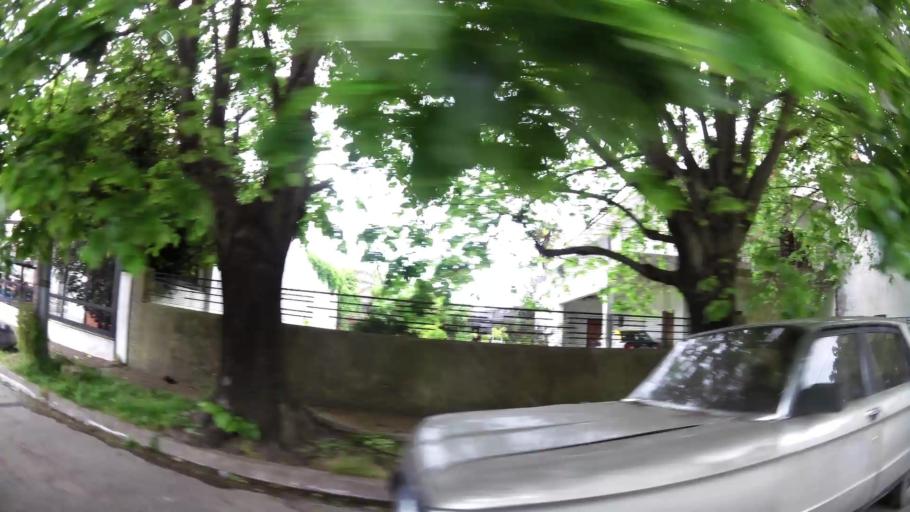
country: AR
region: Buenos Aires
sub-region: Partido de Quilmes
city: Quilmes
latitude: -34.7573
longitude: -58.2178
